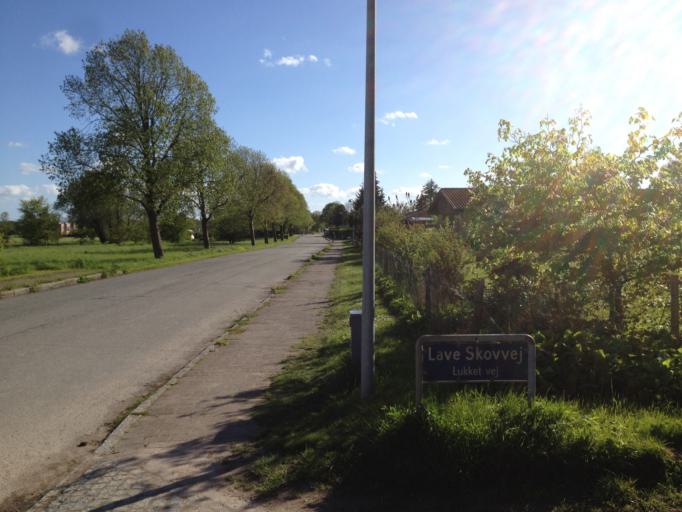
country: DK
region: Capital Region
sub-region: Fredensborg Kommune
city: Niva
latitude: 55.9407
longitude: 12.5211
